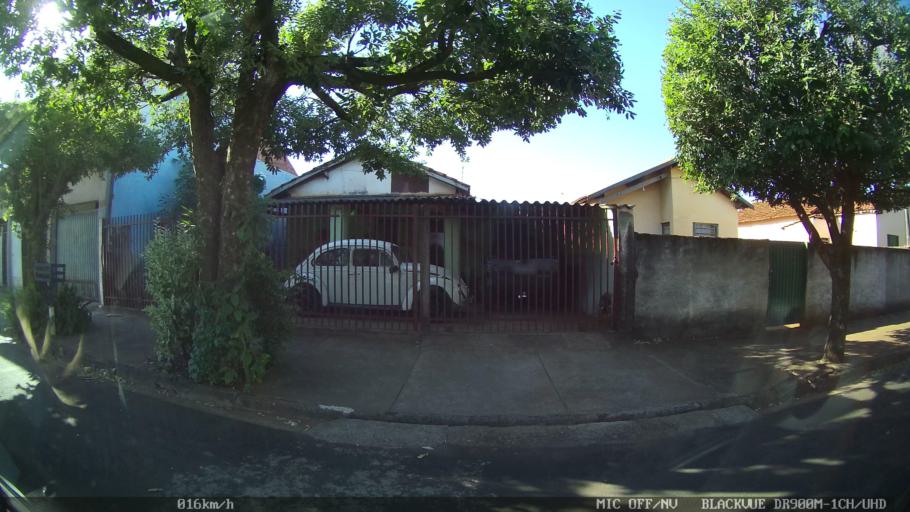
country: BR
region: Sao Paulo
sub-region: Olimpia
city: Olimpia
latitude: -20.7423
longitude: -48.8914
